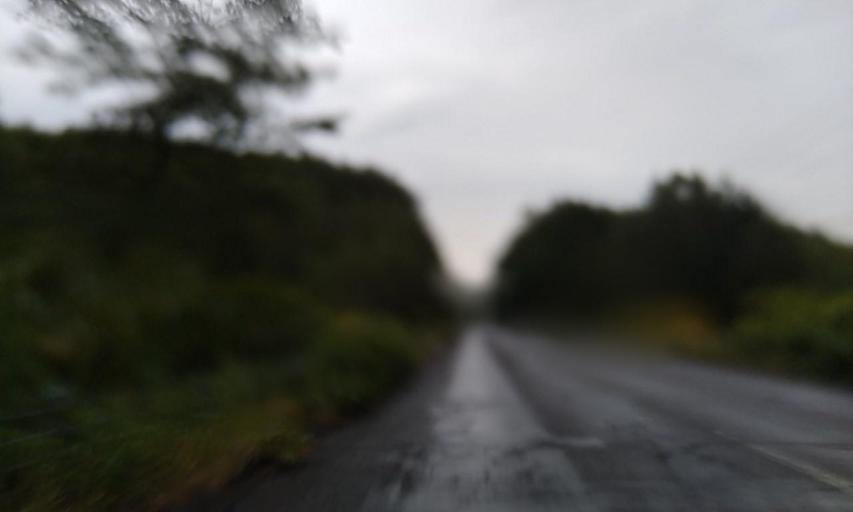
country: JP
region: Hokkaido
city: Mombetsu
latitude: 44.4815
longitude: 143.1057
